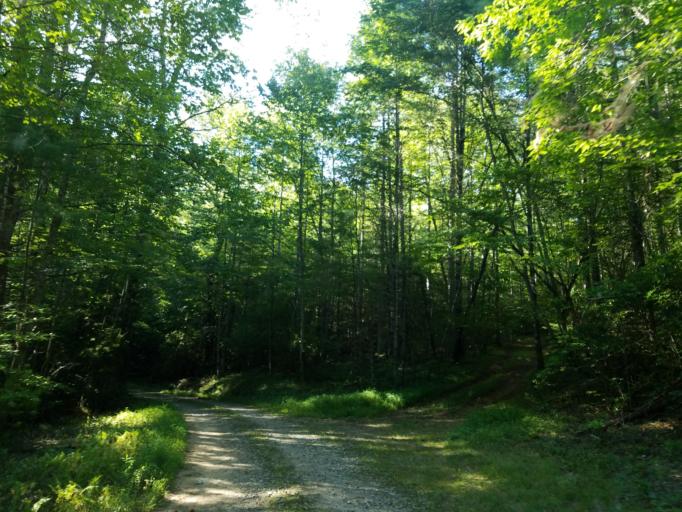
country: US
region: Georgia
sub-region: Union County
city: Blairsville
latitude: 34.7624
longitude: -84.1142
